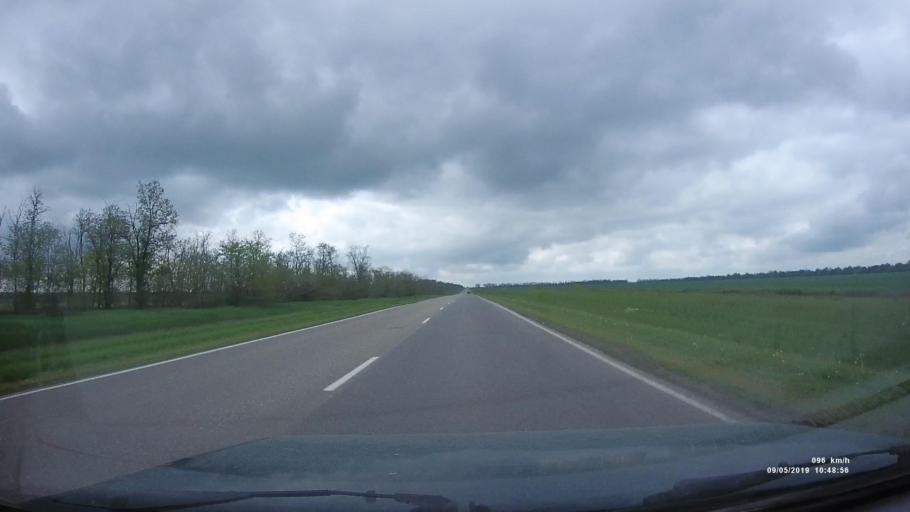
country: RU
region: Rostov
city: Peshkovo
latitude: 46.9495
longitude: 39.3555
